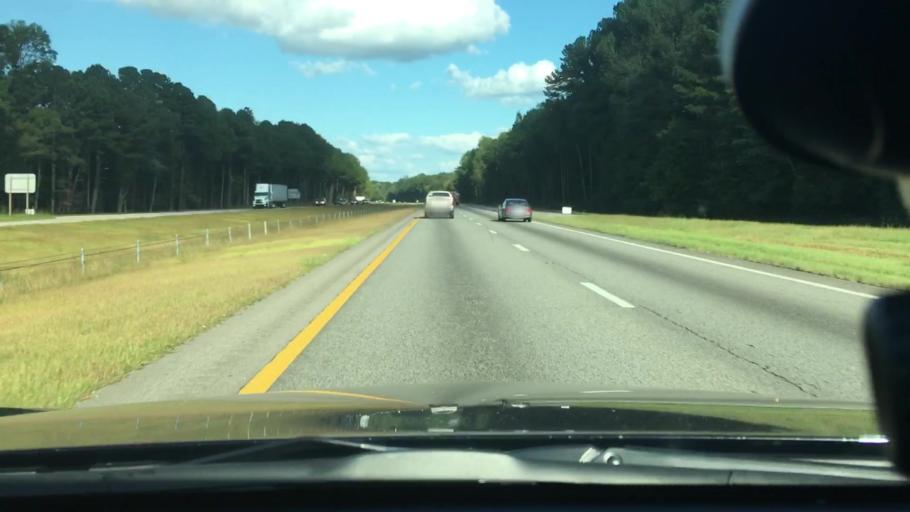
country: US
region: North Carolina
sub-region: Wake County
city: Wendell
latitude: 35.8252
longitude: -78.3724
